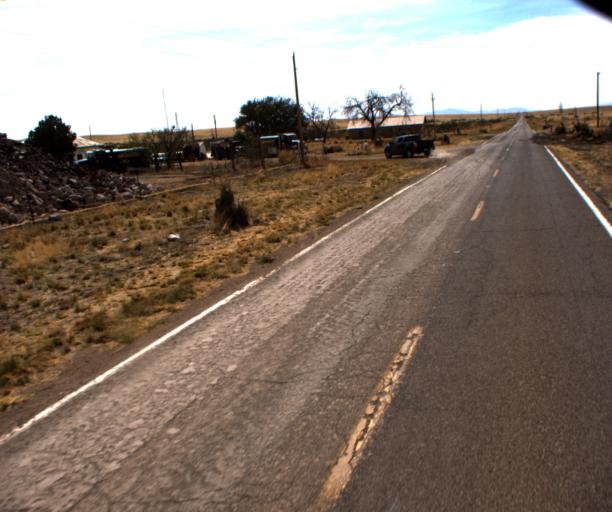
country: US
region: Arizona
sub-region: Cochise County
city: Willcox
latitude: 32.0067
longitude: -109.4047
